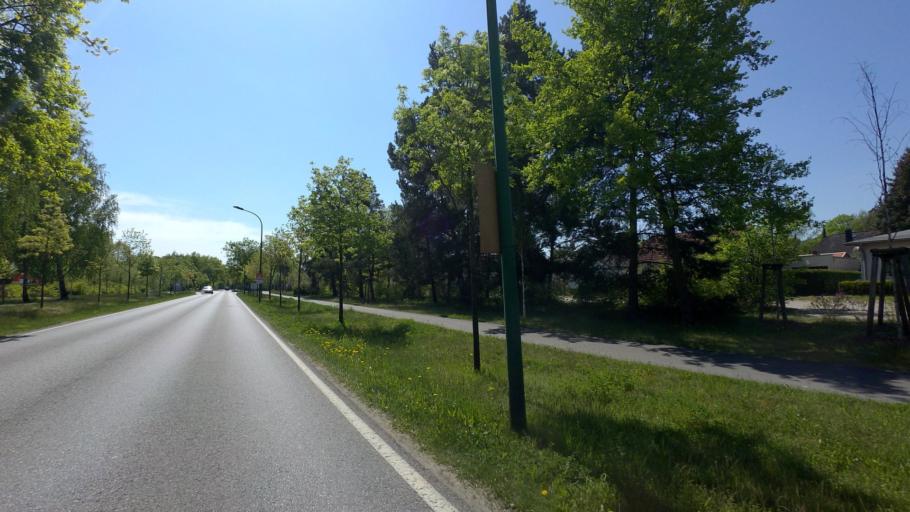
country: DE
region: Brandenburg
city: Bestensee
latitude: 52.2705
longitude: 13.6330
